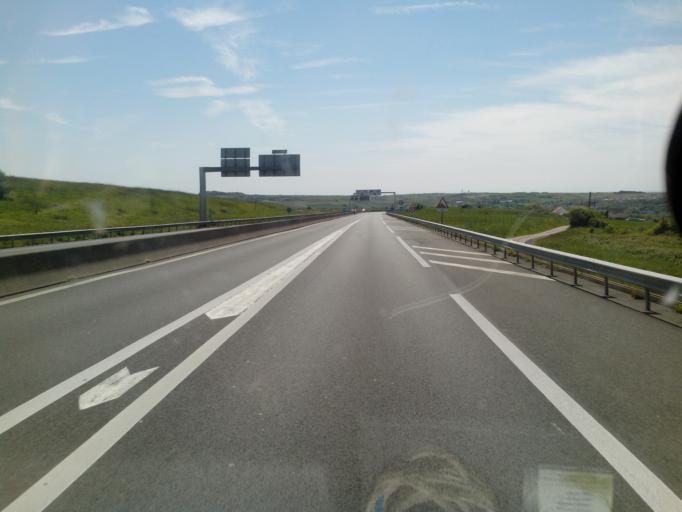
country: FR
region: Nord-Pas-de-Calais
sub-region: Departement du Pas-de-Calais
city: Saint-Leonard
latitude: 50.7065
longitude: 1.6327
